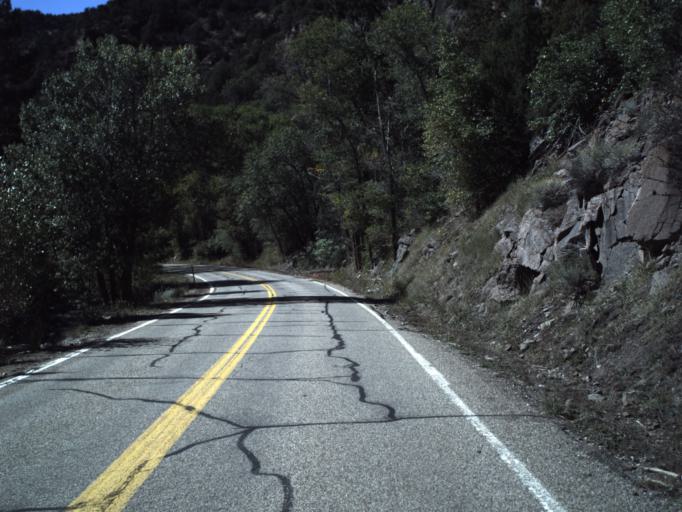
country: US
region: Utah
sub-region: Beaver County
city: Beaver
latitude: 38.2632
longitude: -112.4978
